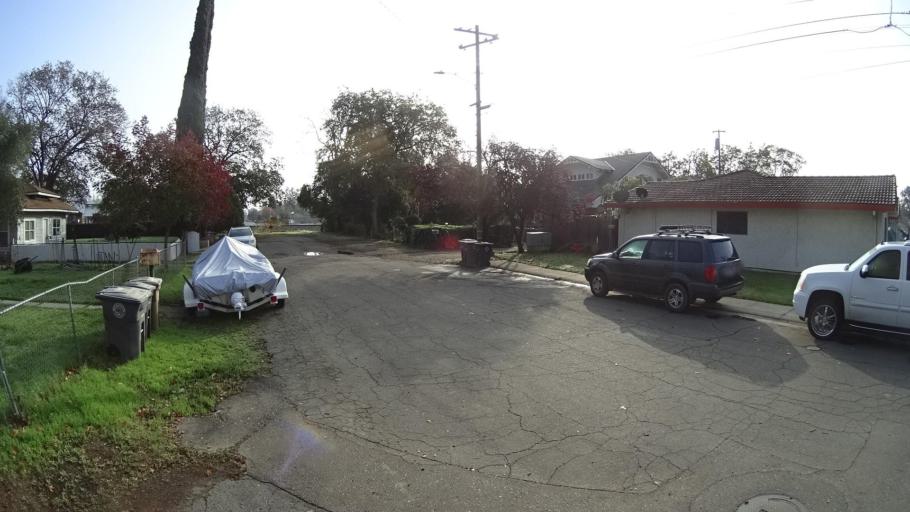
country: US
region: California
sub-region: Sacramento County
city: Elk Grove
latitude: 38.4079
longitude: -121.3650
